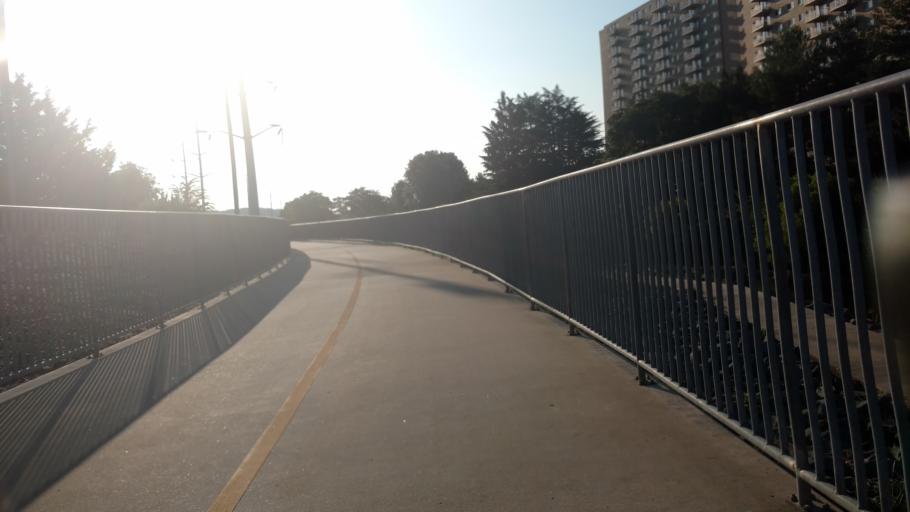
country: US
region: Virginia
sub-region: Arlington County
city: Arlington
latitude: 38.8431
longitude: -77.0817
